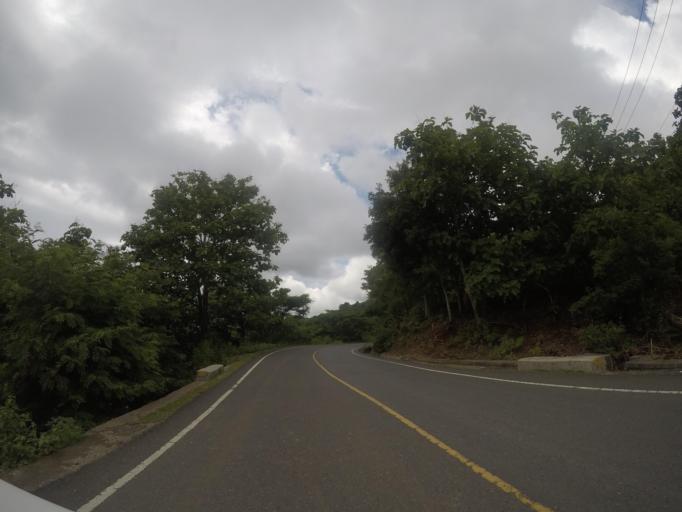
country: TL
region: Bobonaro
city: Maliana
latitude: -8.9645
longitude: 125.0371
